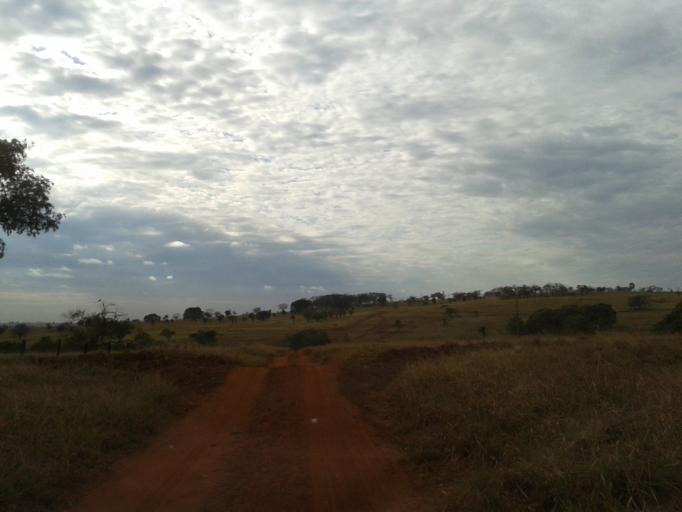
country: BR
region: Minas Gerais
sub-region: Santa Vitoria
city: Santa Vitoria
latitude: -18.7336
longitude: -50.2395
